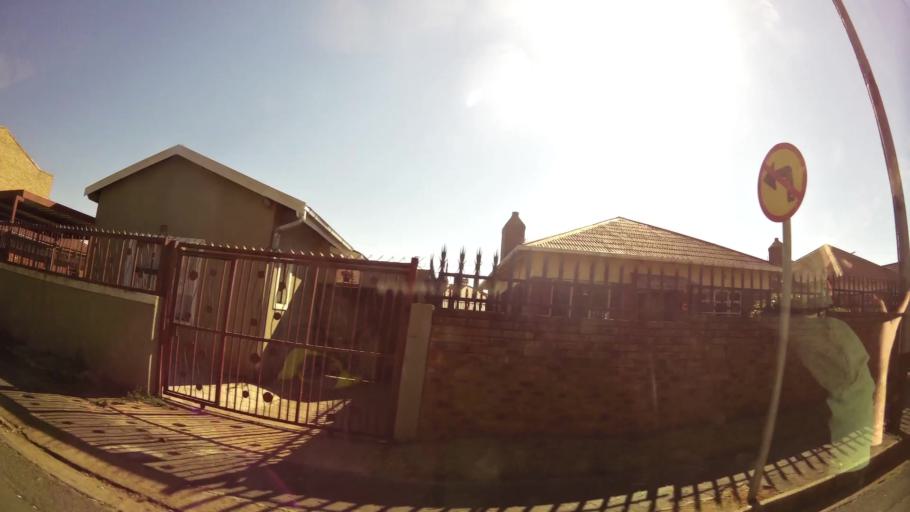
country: ZA
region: Gauteng
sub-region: City of Johannesburg Metropolitan Municipality
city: Johannesburg
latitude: -26.1874
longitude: 27.9760
